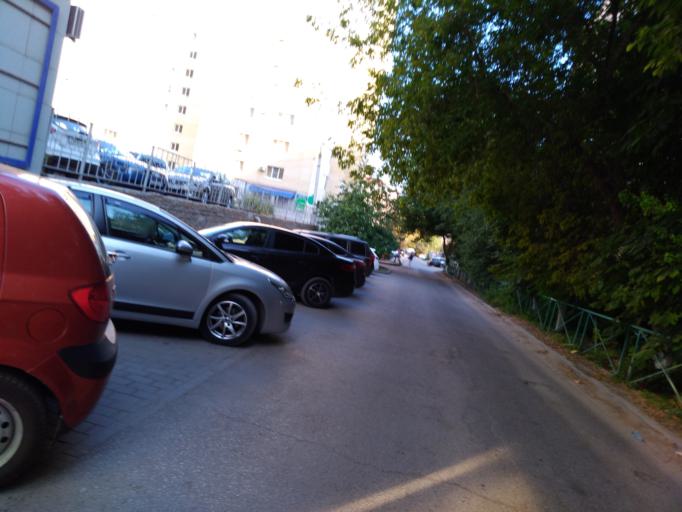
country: RU
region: Volgograd
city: Volgograd
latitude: 48.7207
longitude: 44.5101
